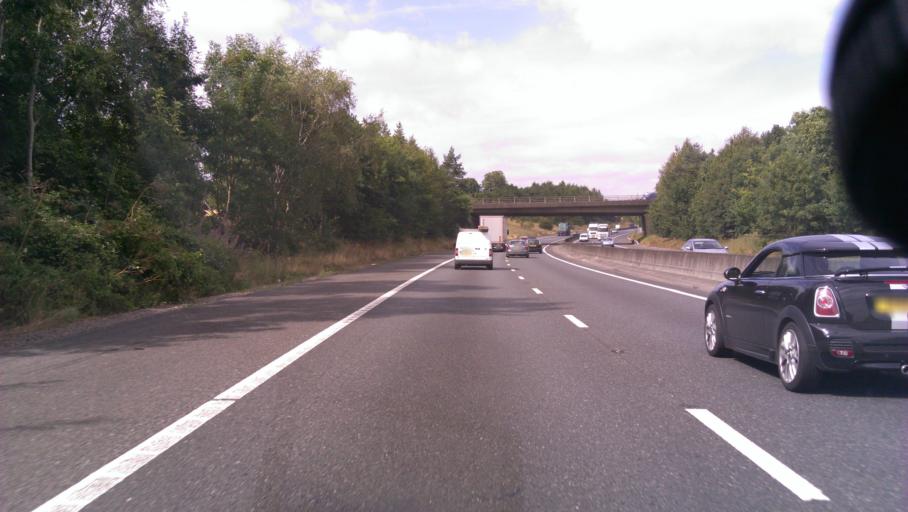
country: GB
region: England
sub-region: Essex
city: Elsenham
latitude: 51.9581
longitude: 0.2134
